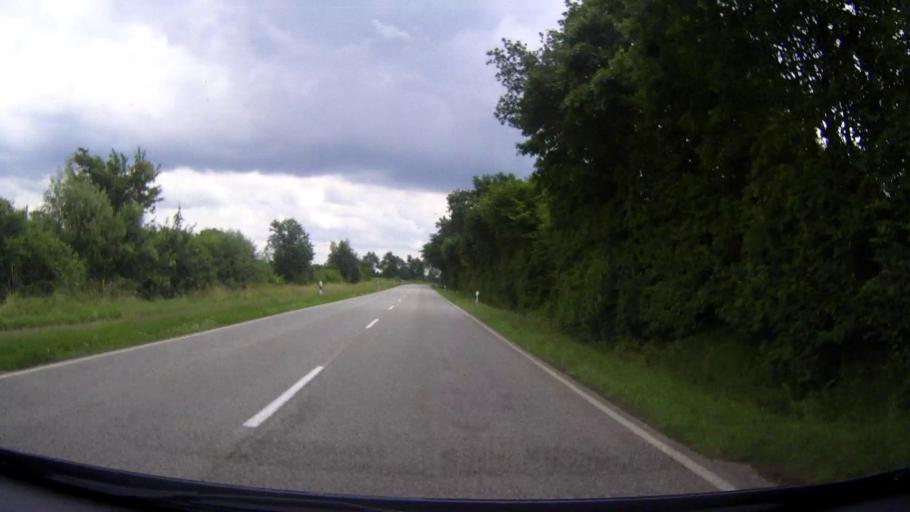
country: DE
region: Schleswig-Holstein
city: Schenefeld
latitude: 54.0654
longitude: 9.4730
